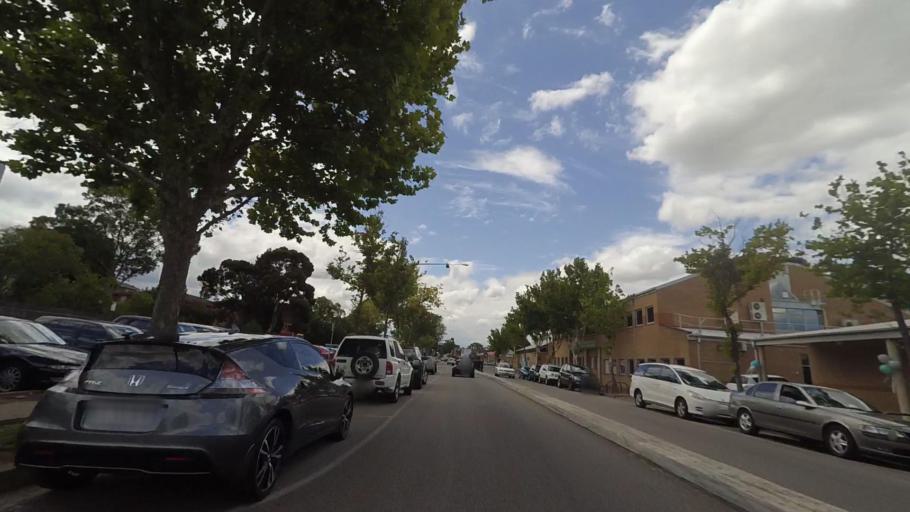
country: AU
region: New South Wales
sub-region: Fairfield
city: Carramar
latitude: -33.8721
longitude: 150.9532
